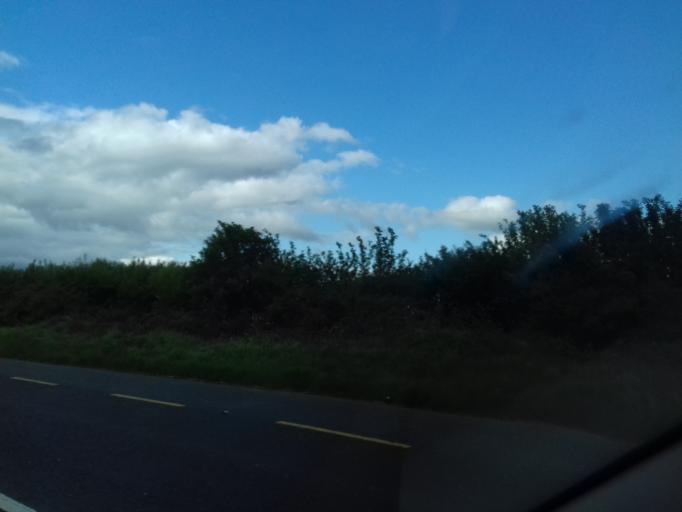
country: IE
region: Leinster
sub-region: Kilkenny
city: Kilkenny
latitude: 52.6085
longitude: -7.2436
